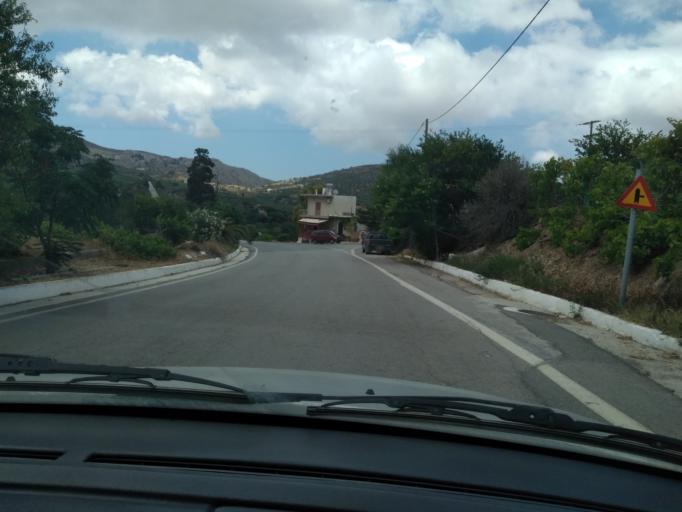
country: GR
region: Crete
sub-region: Nomos Lasithiou
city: Makry-Gialos
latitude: 35.0740
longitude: 26.0470
